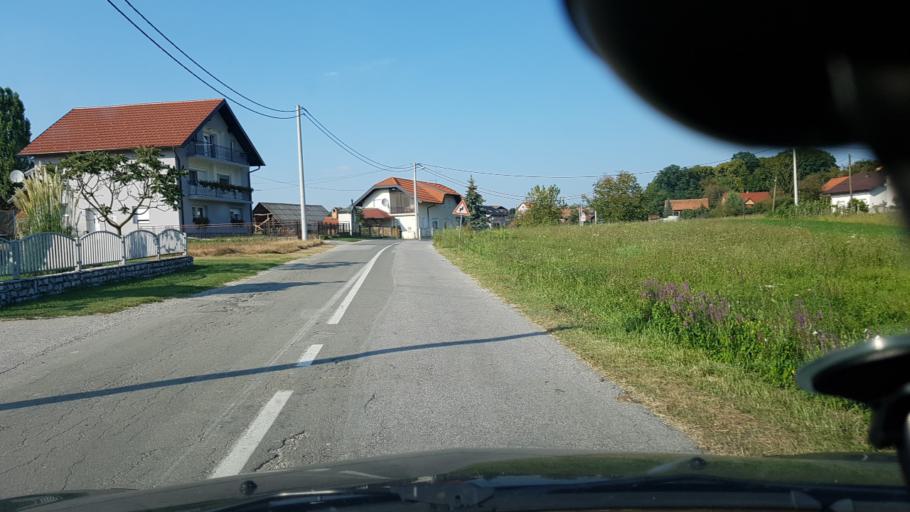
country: HR
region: Zagrebacka
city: Bregana
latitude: 45.9093
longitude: 15.6928
